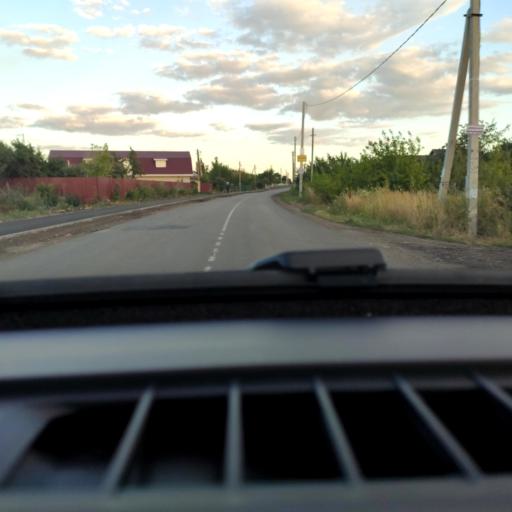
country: RU
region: Voronezj
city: Orlovo
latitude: 51.6674
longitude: 39.6904
